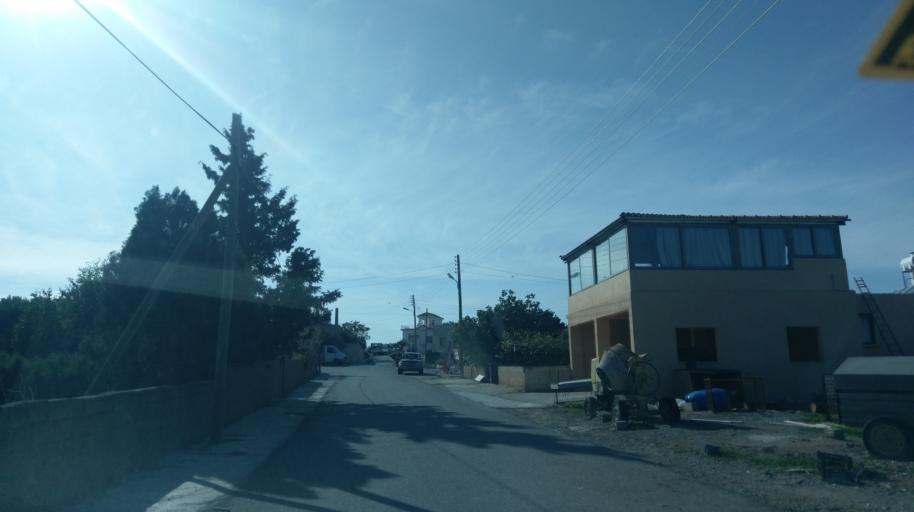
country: CY
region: Ammochostos
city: Trikomo
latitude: 35.3390
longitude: 33.8706
